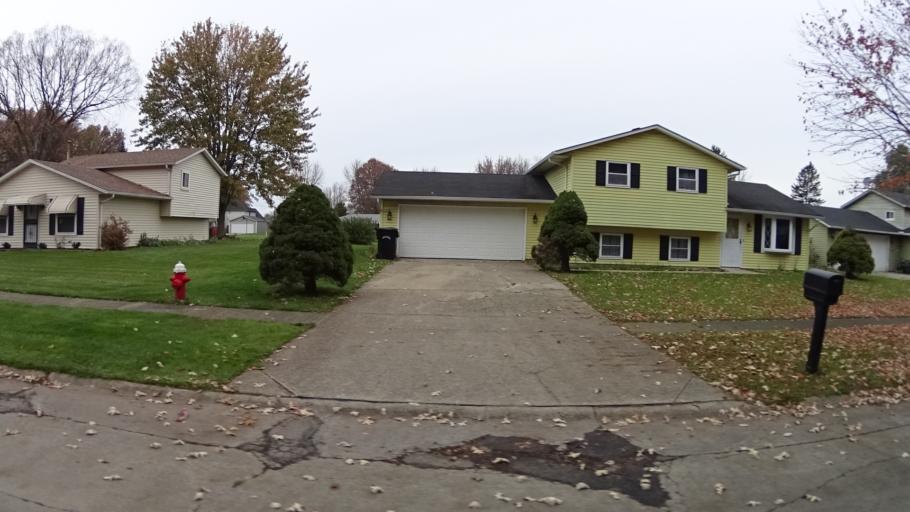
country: US
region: Ohio
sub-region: Lorain County
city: Elyria
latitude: 41.3424
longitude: -82.1068
